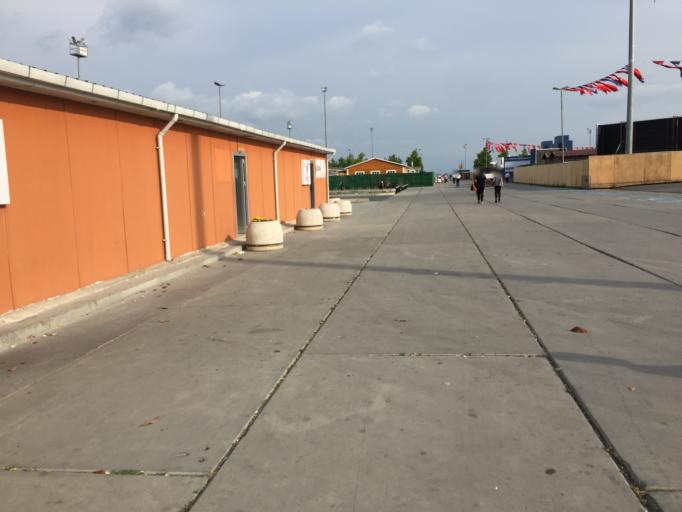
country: TR
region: Istanbul
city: Istanbul
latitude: 41.0003
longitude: 28.9397
